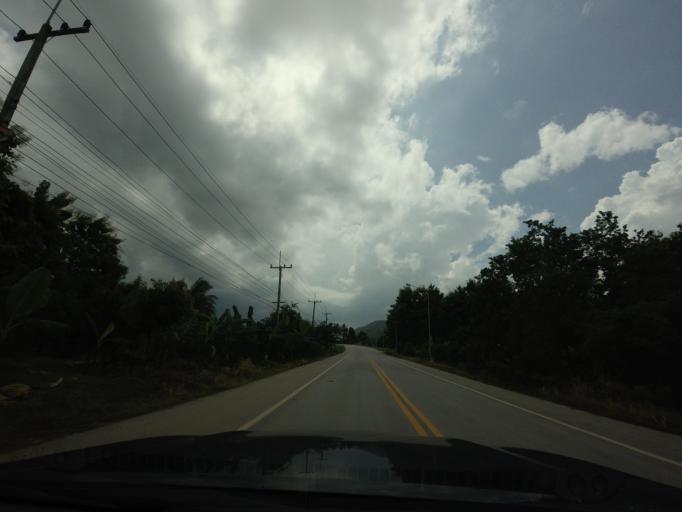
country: TH
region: Loei
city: Pak Chom
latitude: 18.0202
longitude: 101.7625
